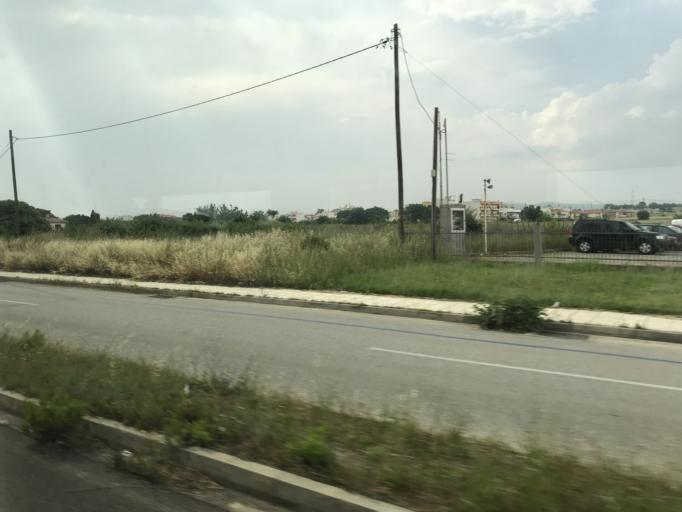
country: GR
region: East Macedonia and Thrace
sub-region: Nomos Evrou
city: Alexandroupoli
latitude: 40.8537
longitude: 25.9134
